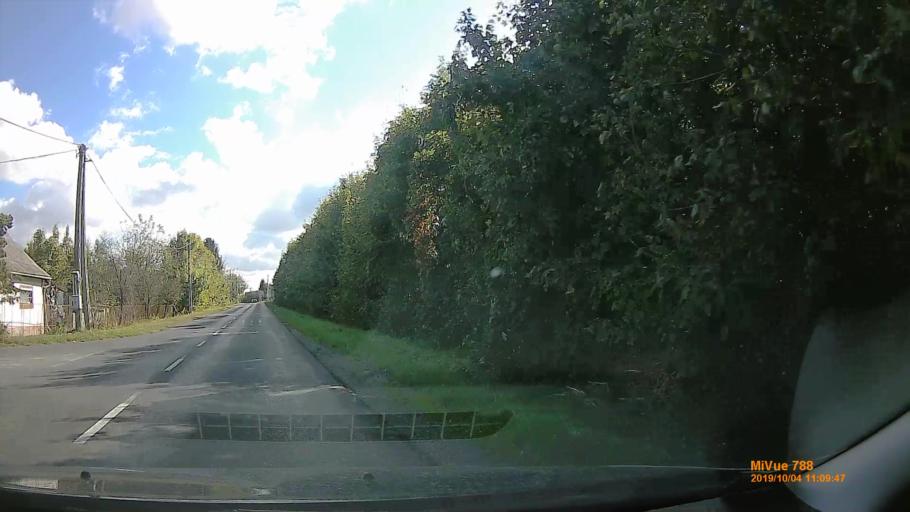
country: HU
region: Somogy
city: Kaposvar
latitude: 46.4133
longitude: 17.7561
